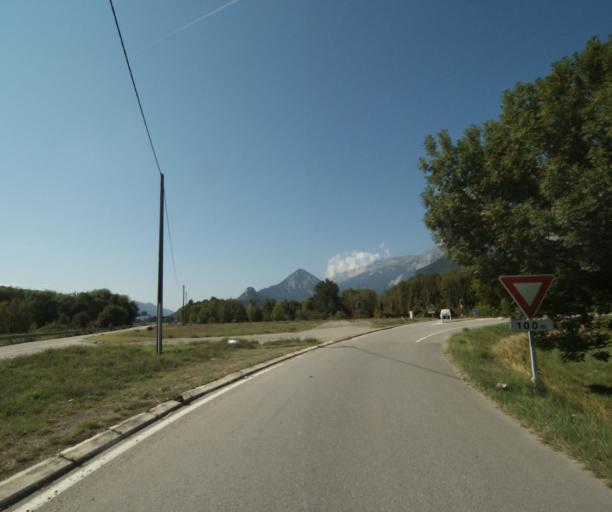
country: FR
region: Rhone-Alpes
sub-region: Departement de l'Isere
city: Allieres-et-Risset
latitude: 45.1062
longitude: 5.6870
